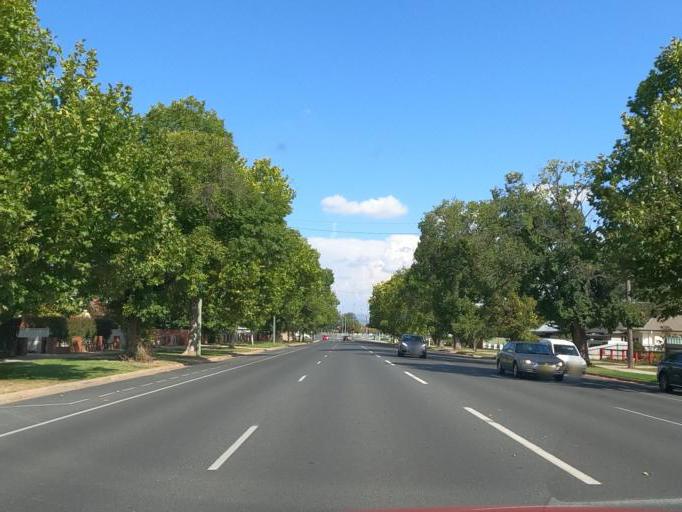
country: AU
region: New South Wales
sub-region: Albury Municipality
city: Albury
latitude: -36.0660
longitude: 146.9243
